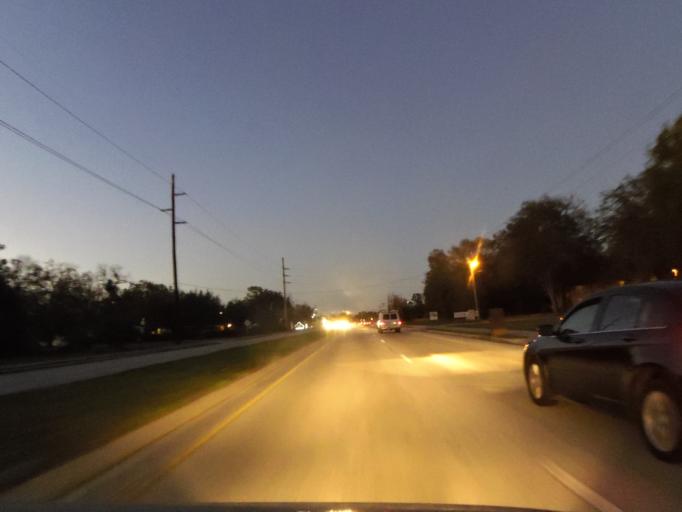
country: US
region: Florida
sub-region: Clay County
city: Lakeside
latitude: 30.1339
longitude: -81.7743
